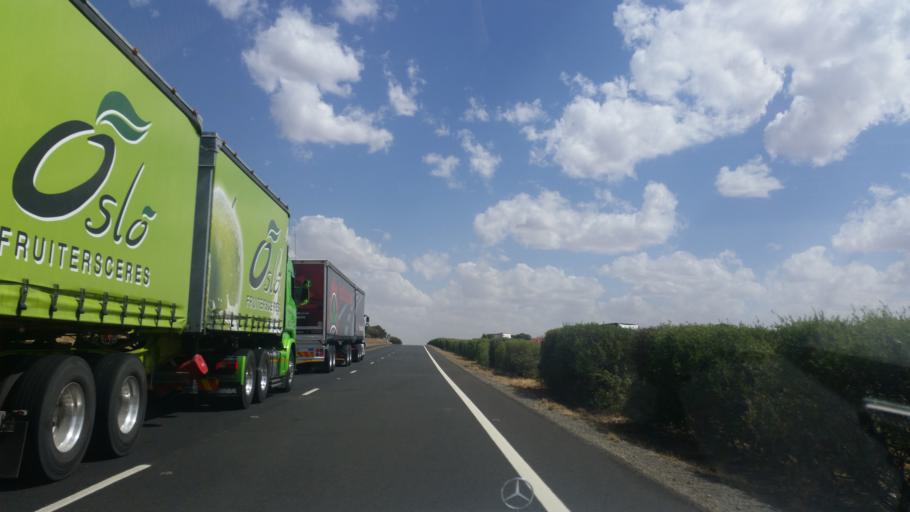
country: ZA
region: Orange Free State
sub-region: Mangaung Metropolitan Municipality
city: Bloemfontein
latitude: -29.0912
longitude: 26.1707
